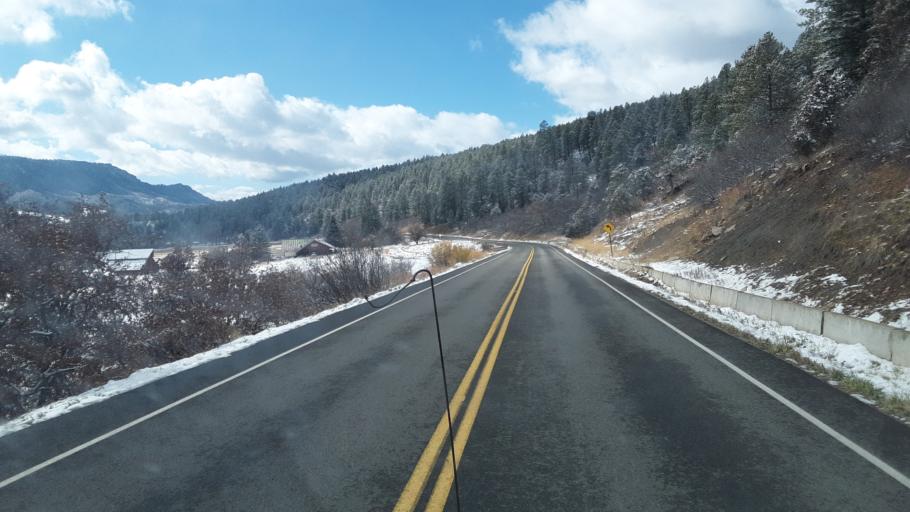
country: US
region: Colorado
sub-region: La Plata County
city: Bayfield
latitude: 37.3456
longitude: -107.7145
